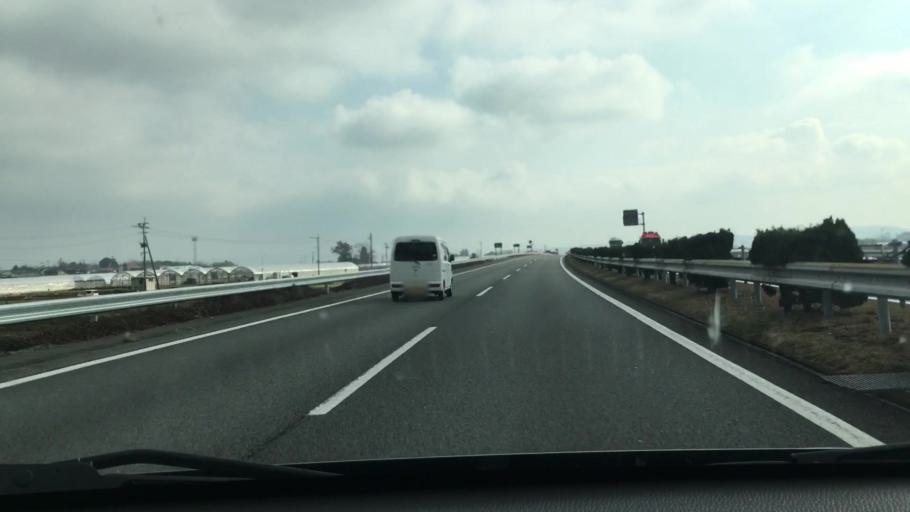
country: JP
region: Kumamoto
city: Ueki
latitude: 32.8837
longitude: 130.7263
